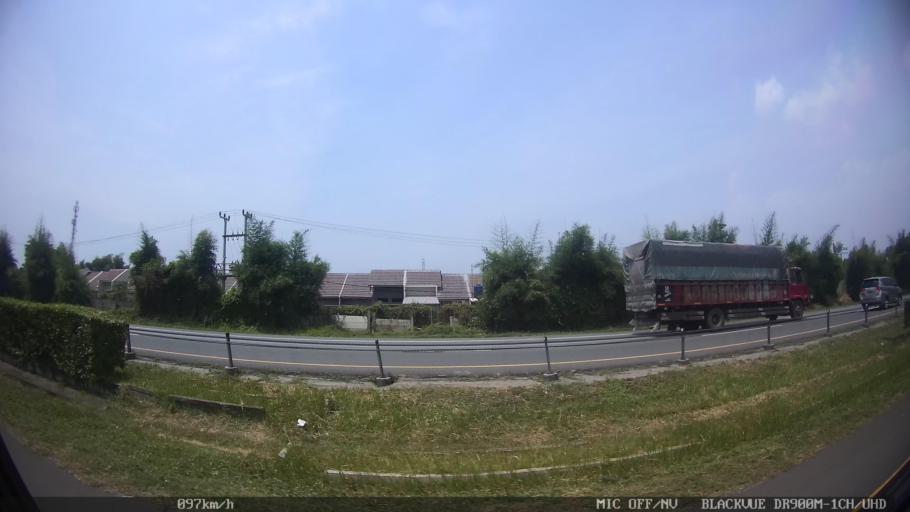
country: ID
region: Banten
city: Serang
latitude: -6.0631
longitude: 106.1241
